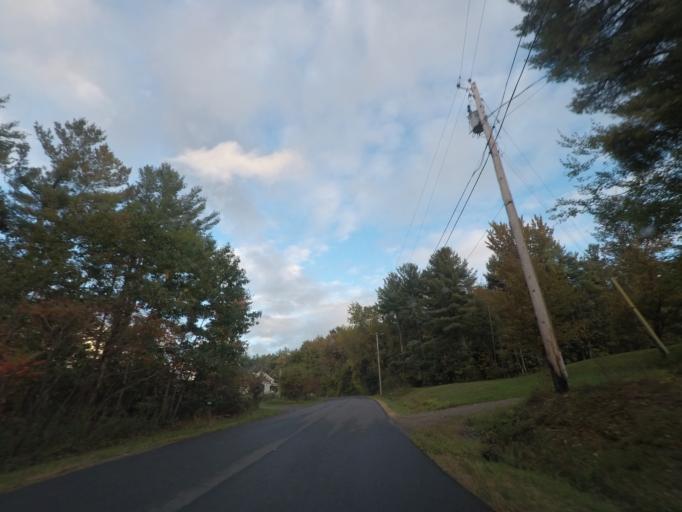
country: US
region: New York
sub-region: Rensselaer County
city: Nassau
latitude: 42.5564
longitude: -73.6121
